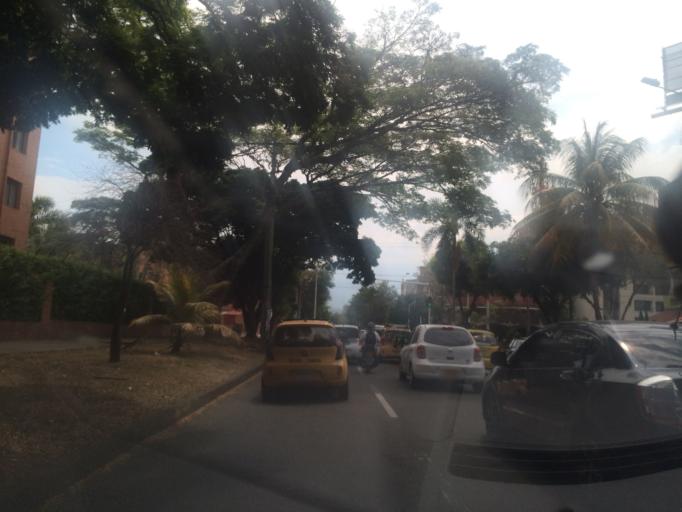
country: CO
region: Valle del Cauca
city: Cali
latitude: 3.3805
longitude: -76.5281
